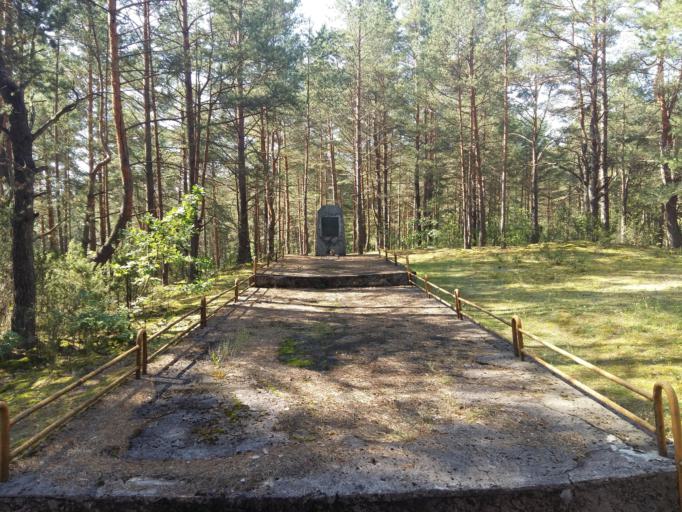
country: LT
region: Alytaus apskritis
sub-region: Alytaus rajonas
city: Daugai
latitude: 54.1581
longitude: 24.1909
